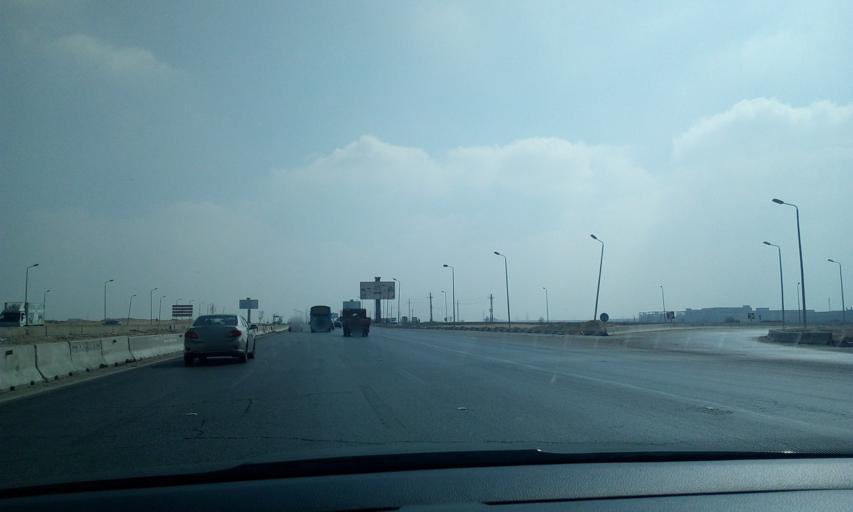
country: EG
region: Eastern Province
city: Bilbays
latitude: 30.2250
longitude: 31.6972
